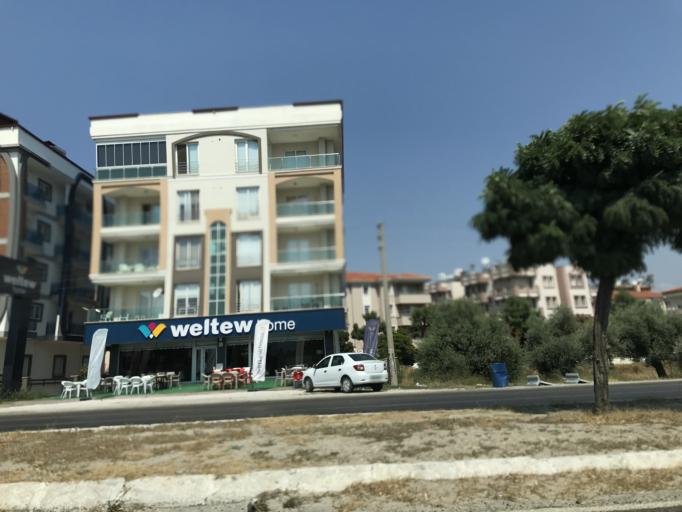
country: TR
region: Mugla
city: Milas
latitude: 37.3053
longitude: 27.7852
